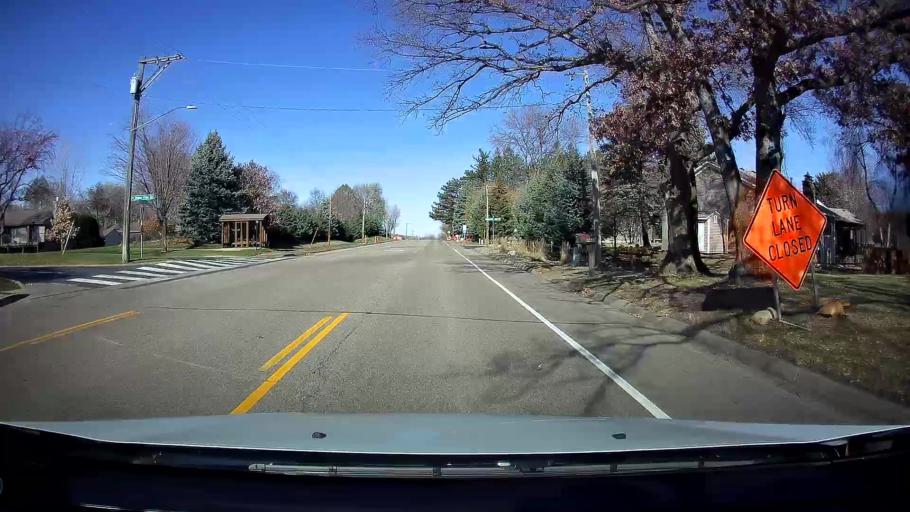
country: US
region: Minnesota
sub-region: Ramsey County
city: Shoreview
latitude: 45.0753
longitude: -93.1575
